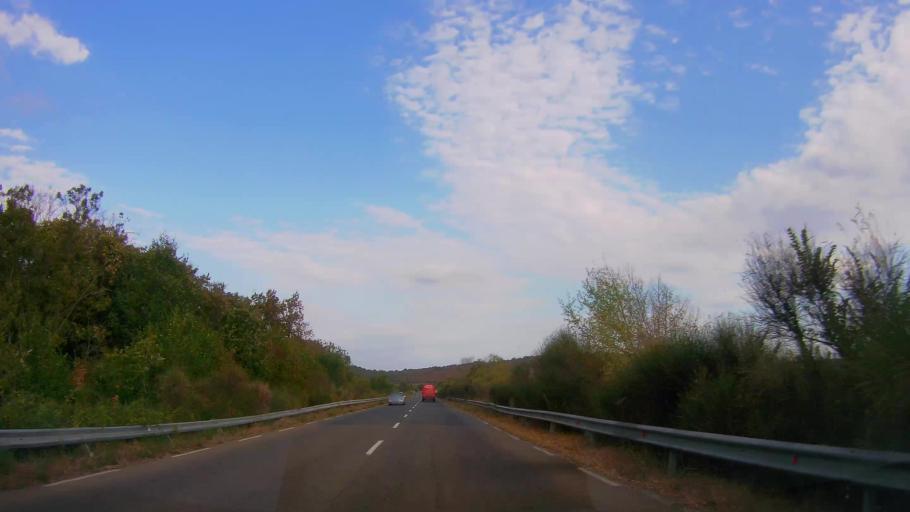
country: BG
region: Burgas
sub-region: Obshtina Sozopol
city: Sozopol
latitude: 42.3585
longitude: 27.7030
